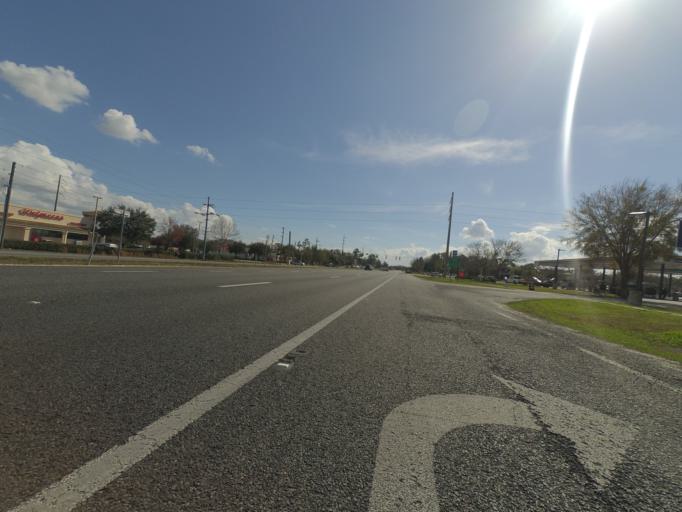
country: US
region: Florida
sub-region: Lake County
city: Eustis
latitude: 28.8763
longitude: -81.6879
